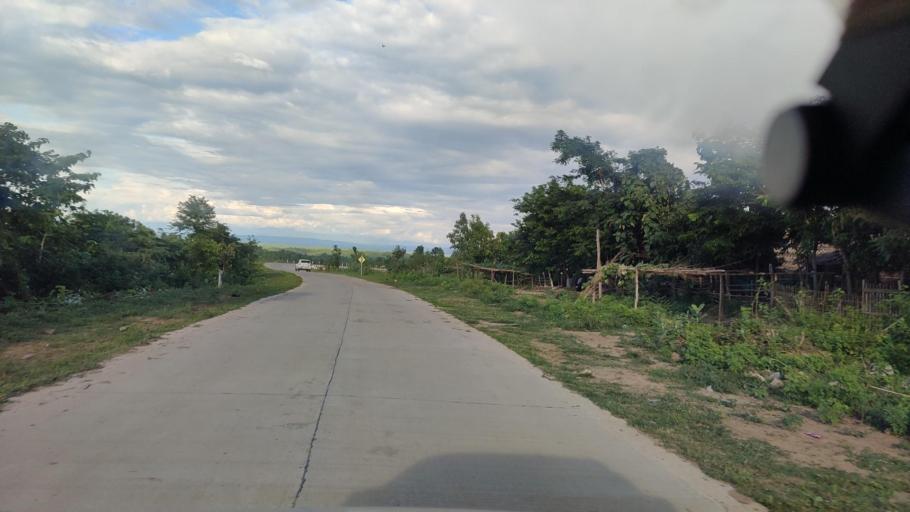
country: MM
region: Magway
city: Taungdwingyi
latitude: 20.0236
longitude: 95.8228
